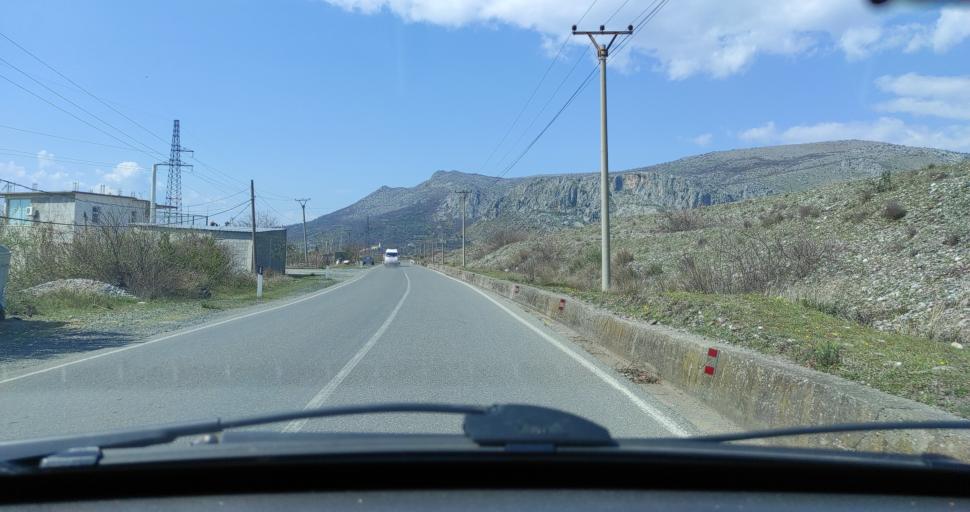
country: AL
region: Shkoder
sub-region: Rrethi i Shkodres
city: Vau i Dejes
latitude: 42.0041
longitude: 19.6249
